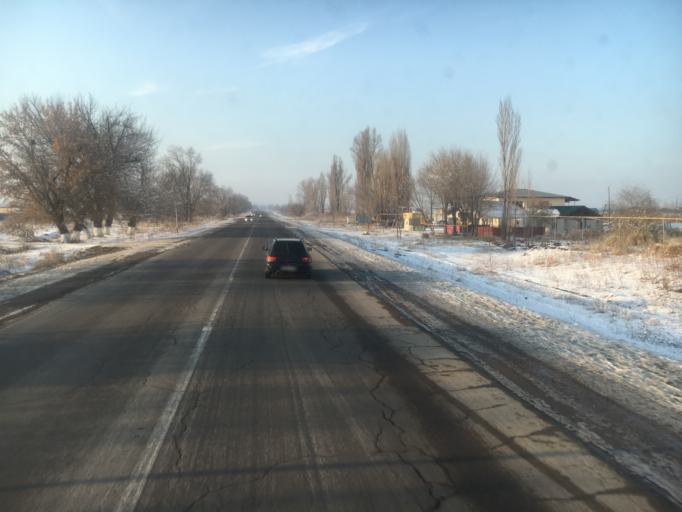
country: KZ
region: Almaty Oblysy
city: Burunday
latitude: 43.3424
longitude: 76.6572
